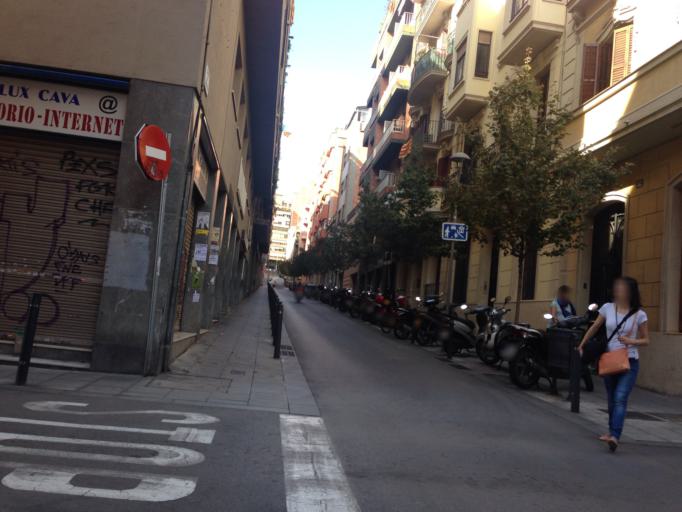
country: ES
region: Catalonia
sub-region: Provincia de Barcelona
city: Gracia
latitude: 41.4081
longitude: 2.1576
